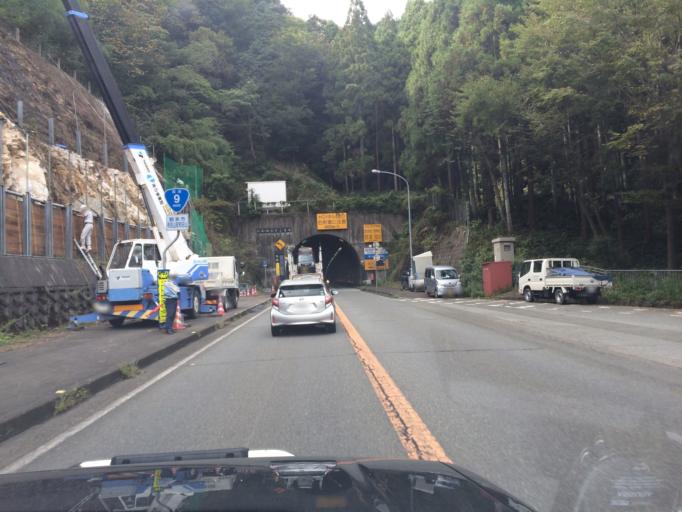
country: JP
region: Hyogo
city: Toyooka
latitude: 35.3363
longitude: 134.8553
